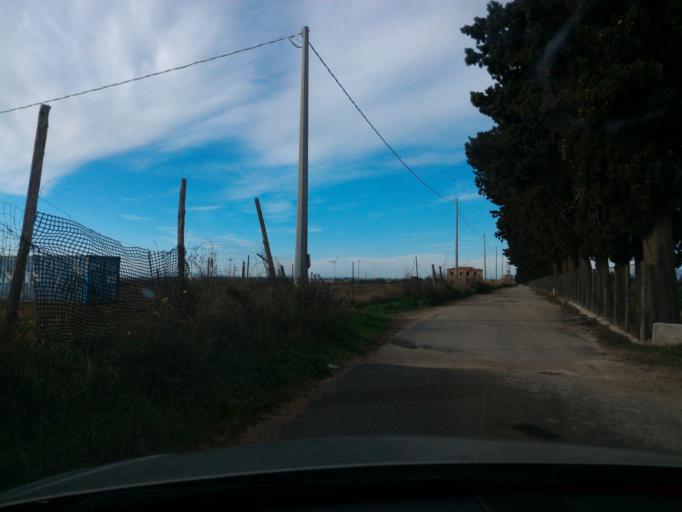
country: IT
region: Calabria
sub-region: Provincia di Crotone
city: Isola di Capo Rizzuto
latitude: 38.9877
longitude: 17.0767
